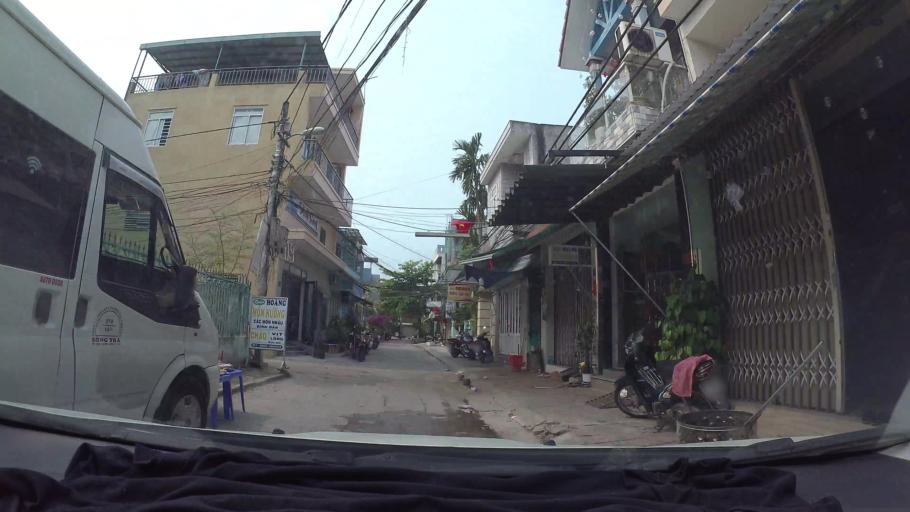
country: VN
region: Da Nang
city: Son Tra
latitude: 16.0424
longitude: 108.2153
